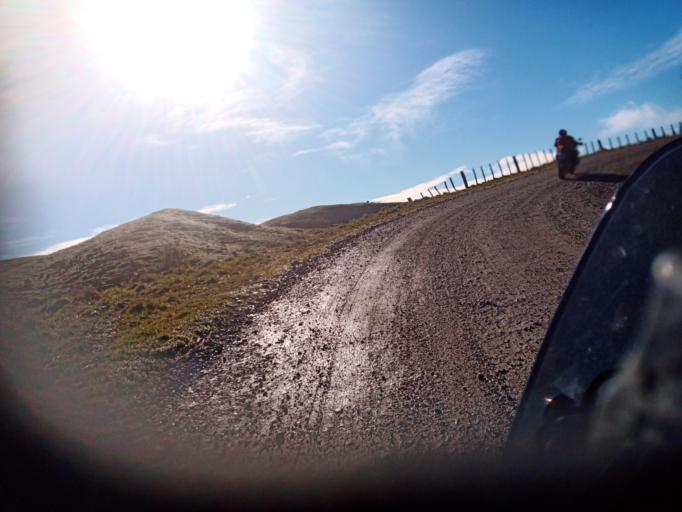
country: NZ
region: Gisborne
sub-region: Gisborne District
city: Gisborne
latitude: -38.1929
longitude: 178.0807
